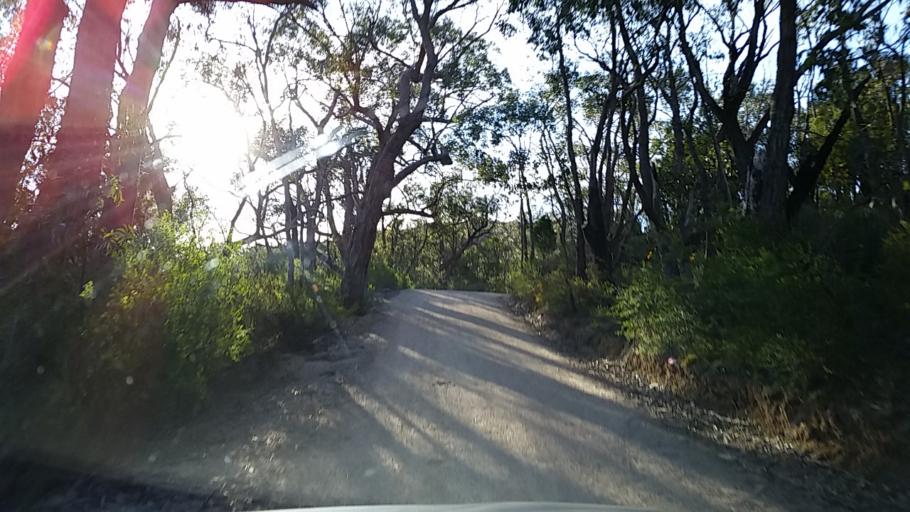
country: AU
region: South Australia
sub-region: Mount Barker
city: Meadows
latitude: -35.2362
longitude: 138.7522
